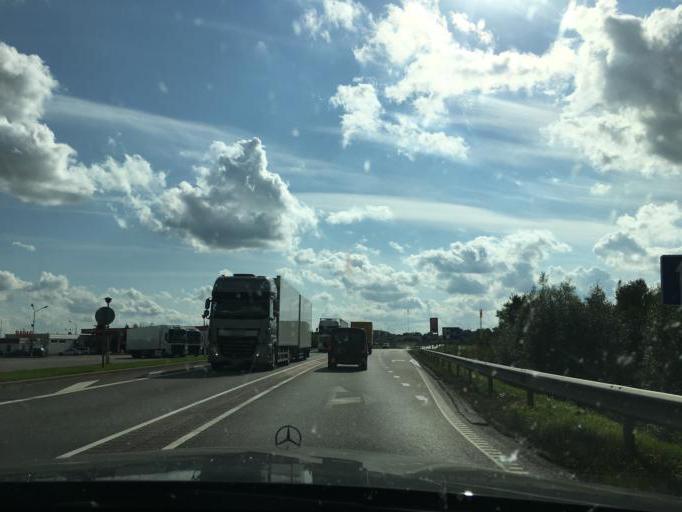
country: LT
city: Kalvarija
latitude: 54.3609
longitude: 23.1837
